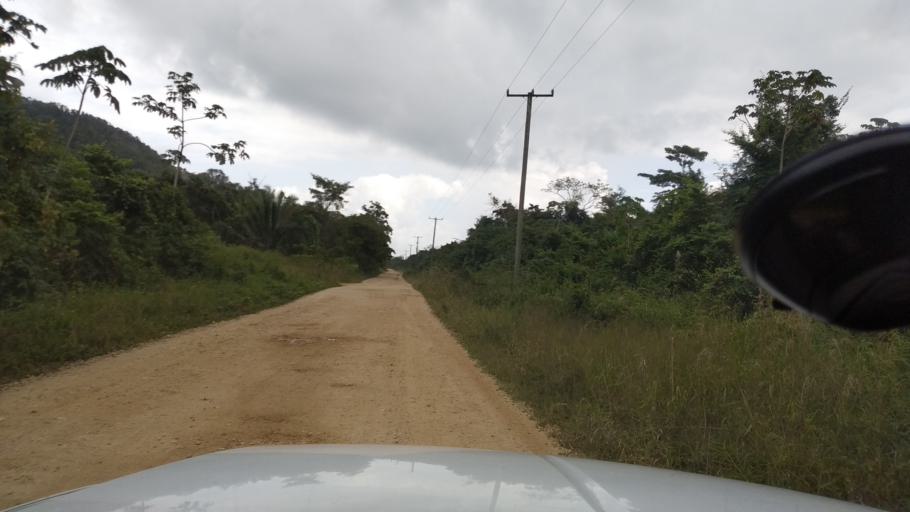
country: BZ
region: Toledo
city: Punta Gorda
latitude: 16.2136
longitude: -89.0143
